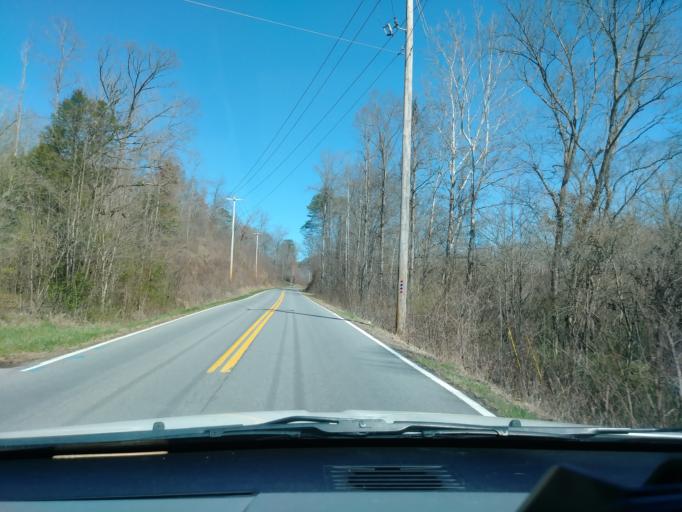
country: US
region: Tennessee
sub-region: Cocke County
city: Newport
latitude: 35.9558
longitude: -83.0495
